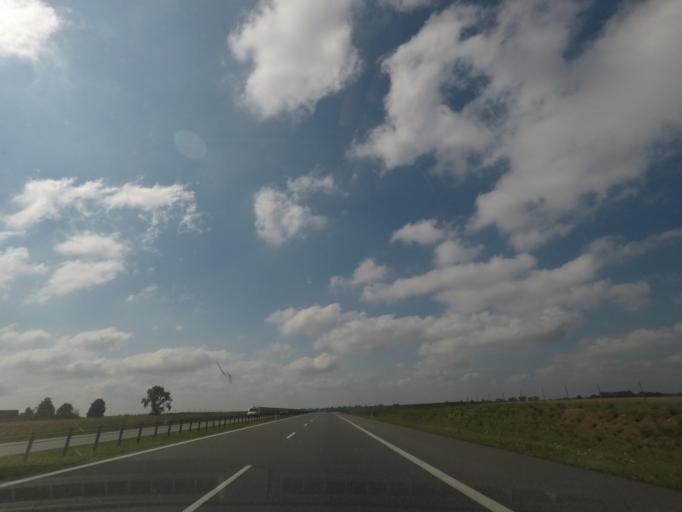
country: PL
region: Kujawsko-Pomorskie
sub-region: Powiat wabrzeski
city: Pluznica
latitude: 53.1939
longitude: 18.7390
